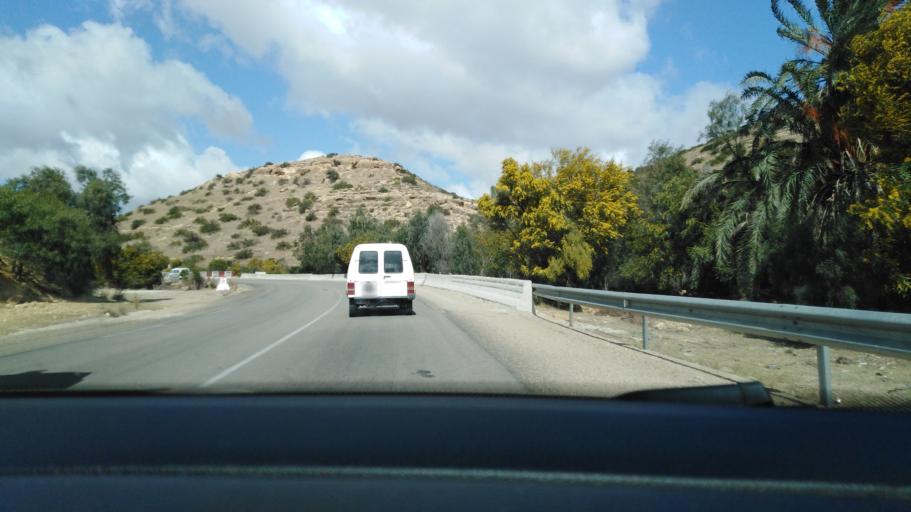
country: TN
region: Al Qayrawan
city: Haffouz
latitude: 35.6343
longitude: 9.8215
